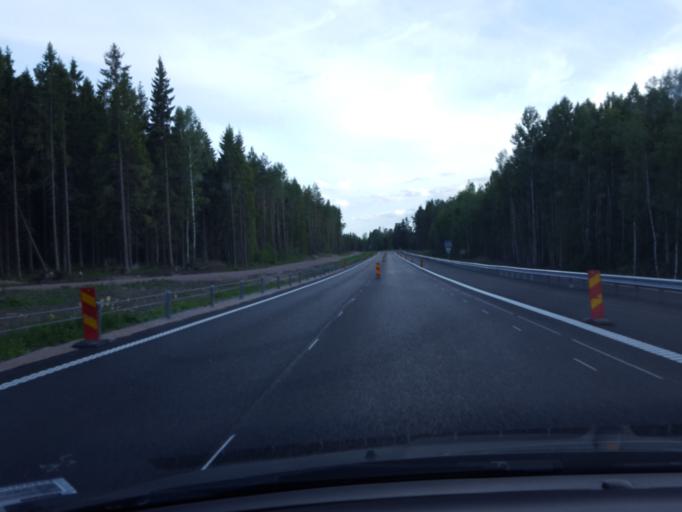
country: SE
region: Uppsala
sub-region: Osthammars Kommun
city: Gimo
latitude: 60.1112
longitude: 18.1291
